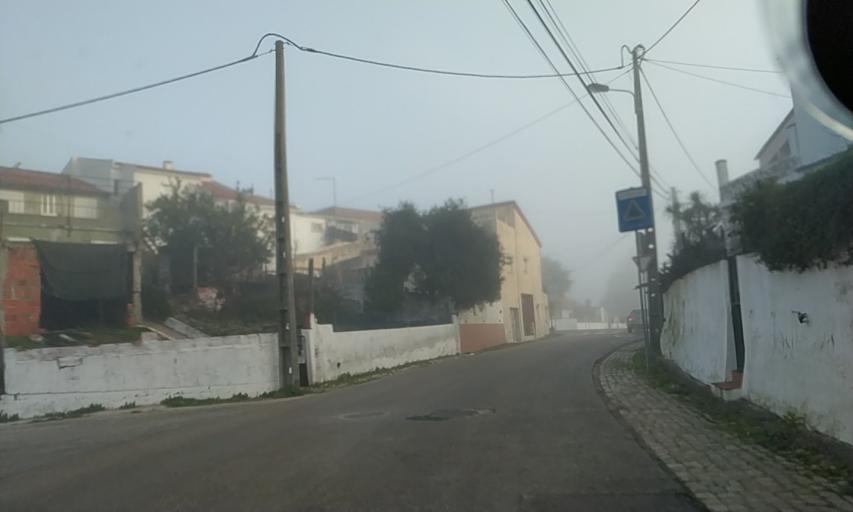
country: PT
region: Setubal
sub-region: Setubal
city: Setubal
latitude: 38.5390
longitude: -8.8480
